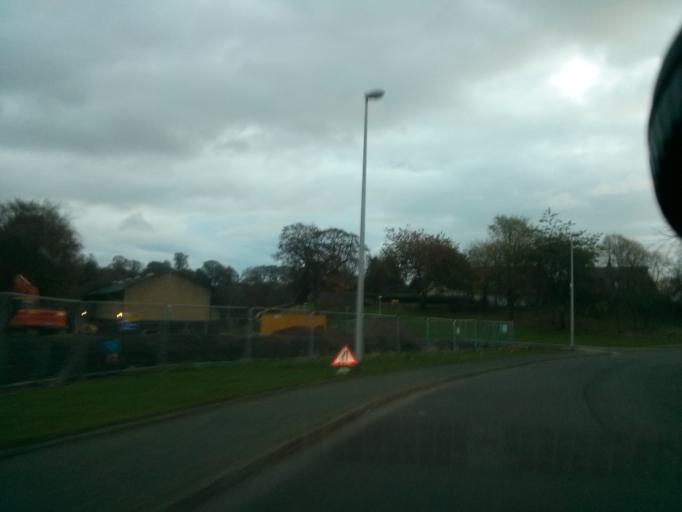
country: GB
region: Scotland
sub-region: Aberdeen City
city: Aberdeen
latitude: 57.1754
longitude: -2.1180
